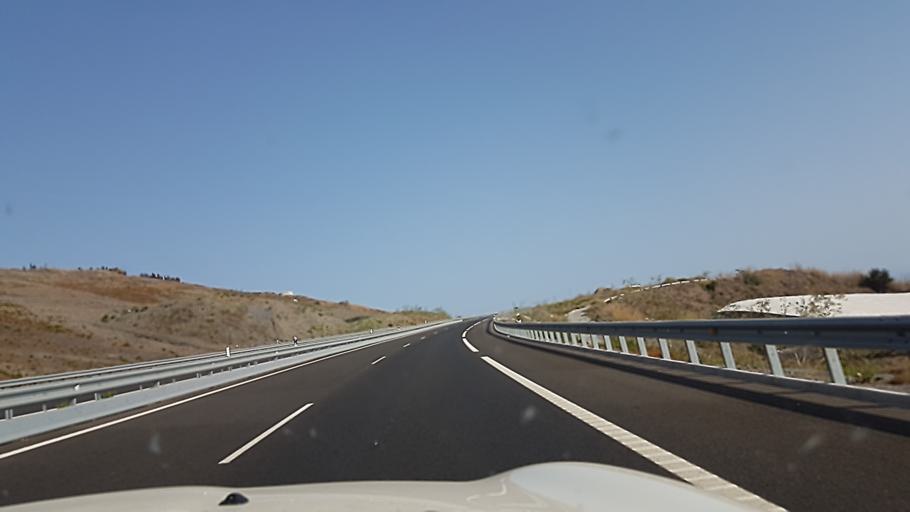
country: ES
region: Andalusia
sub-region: Provincia de Granada
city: Albunol
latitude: 36.7547
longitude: -3.2197
